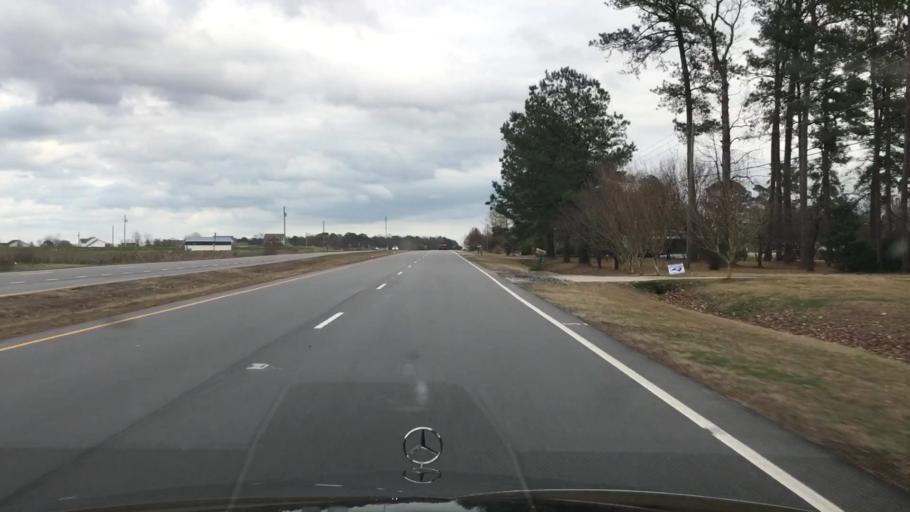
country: US
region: North Carolina
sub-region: Onslow County
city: Richlands
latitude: 34.9174
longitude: -77.6096
